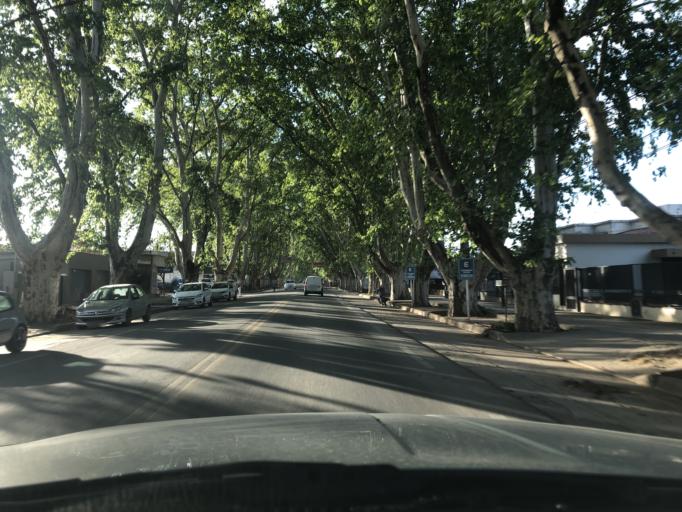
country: AR
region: Cordoba
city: Jesus Maria
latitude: -31.0184
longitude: -64.0651
